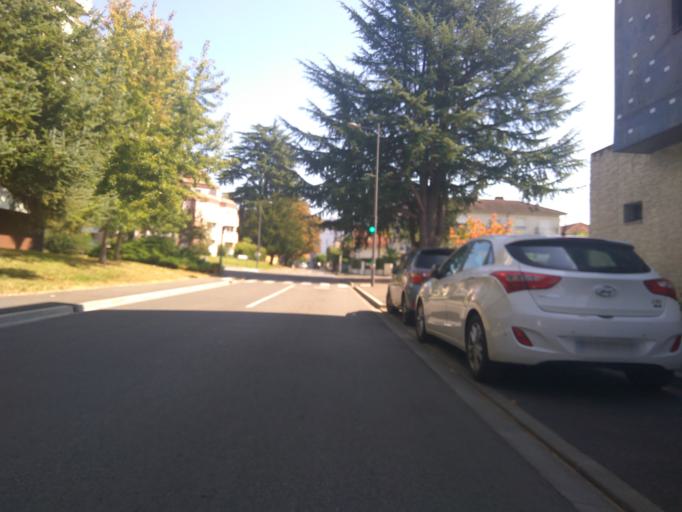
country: FR
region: Aquitaine
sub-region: Departement des Pyrenees-Atlantiques
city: Pau
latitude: 43.3053
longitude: -0.3617
